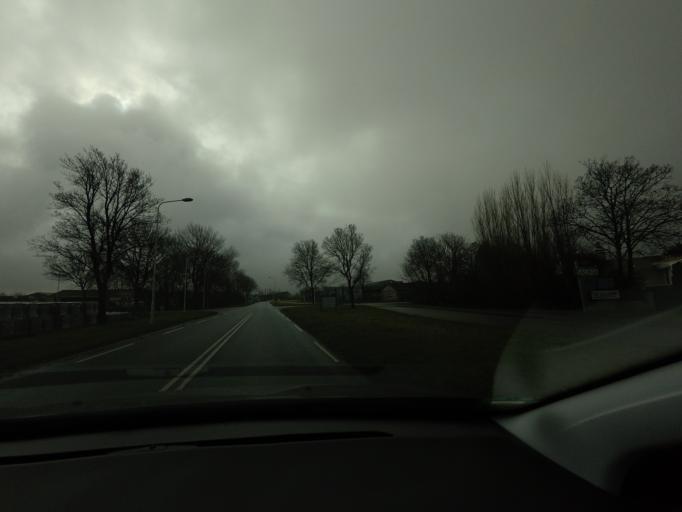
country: NL
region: Friesland
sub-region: Sudwest Fryslan
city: Makkum
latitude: 53.0543
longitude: 5.4099
